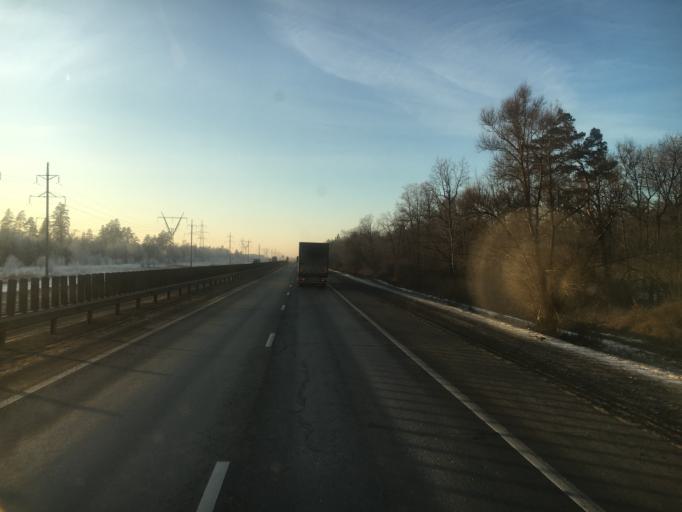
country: RU
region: Samara
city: Pribrezhnyy
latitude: 53.5163
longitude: 49.8594
